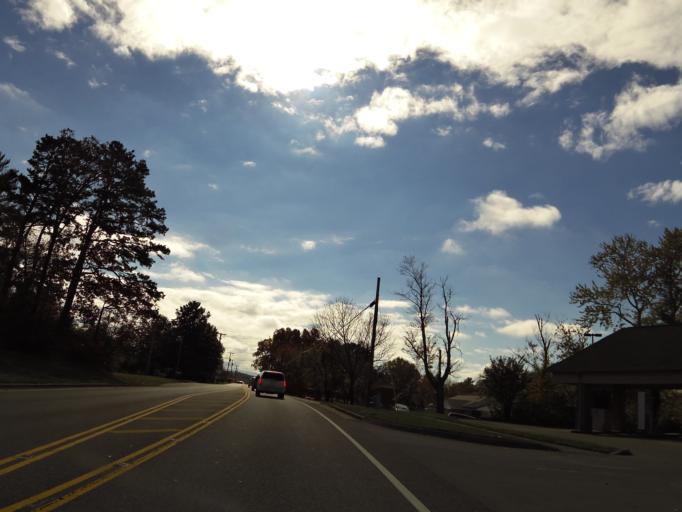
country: US
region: Tennessee
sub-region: Blount County
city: Eagleton Village
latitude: 35.7977
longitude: -83.9456
